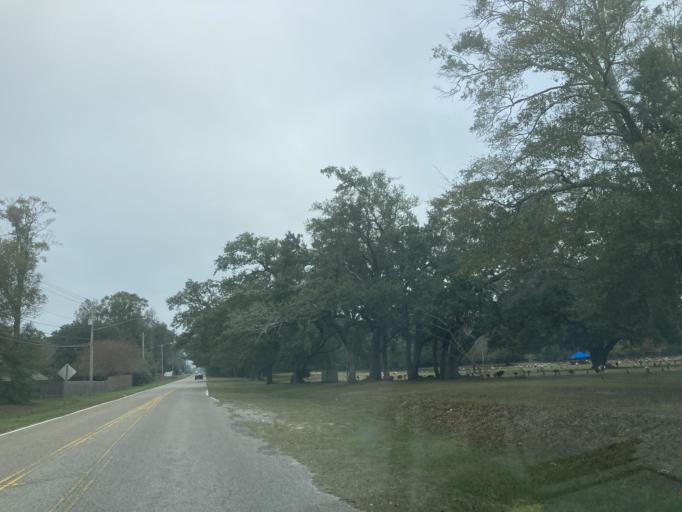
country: US
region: Mississippi
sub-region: Harrison County
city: West Gulfport
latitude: 30.4100
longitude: -89.0312
